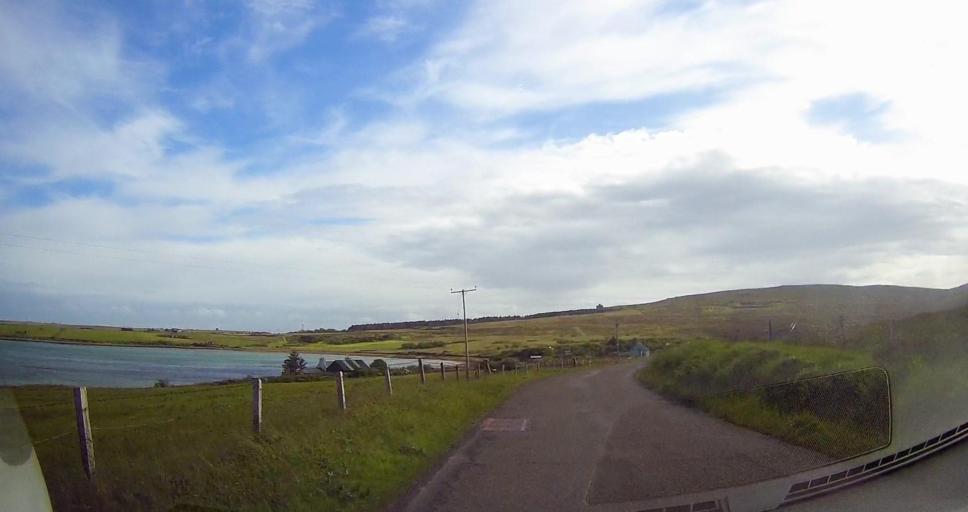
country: GB
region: Scotland
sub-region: Orkney Islands
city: Stromness
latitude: 58.8435
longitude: -3.2105
